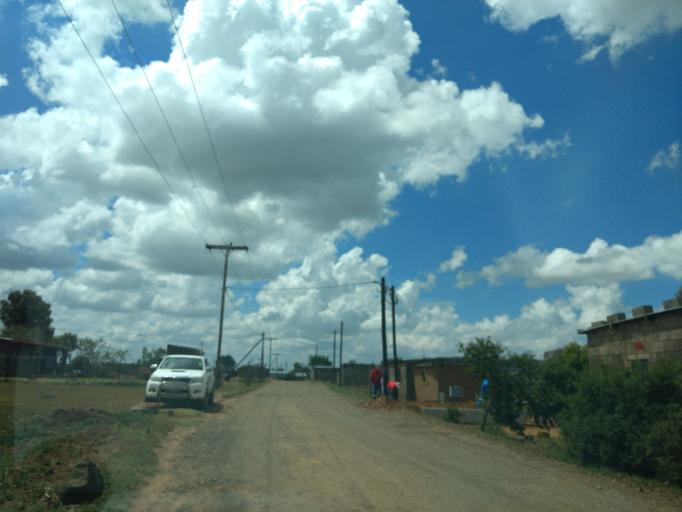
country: LS
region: Maseru
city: Maseru
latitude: -29.3725
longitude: 27.5109
